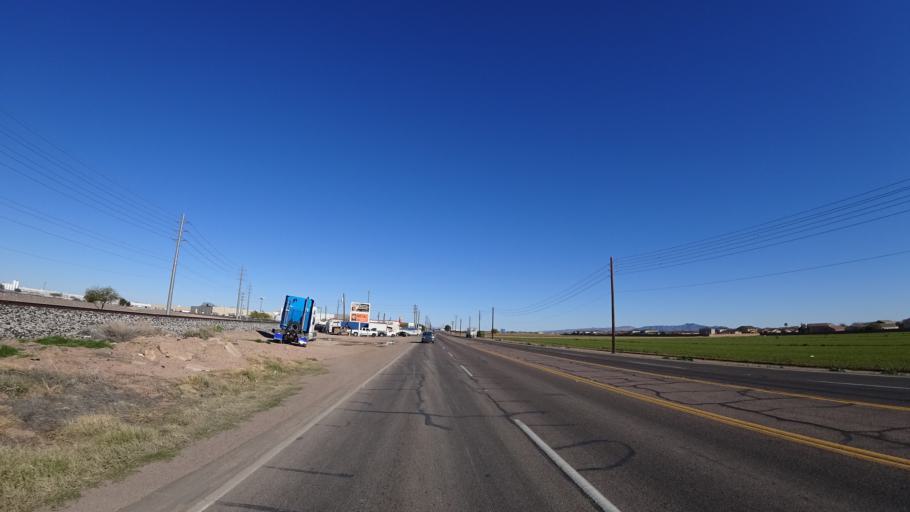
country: US
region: Arizona
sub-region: Maricopa County
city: Tolleson
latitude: 33.4355
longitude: -112.2881
